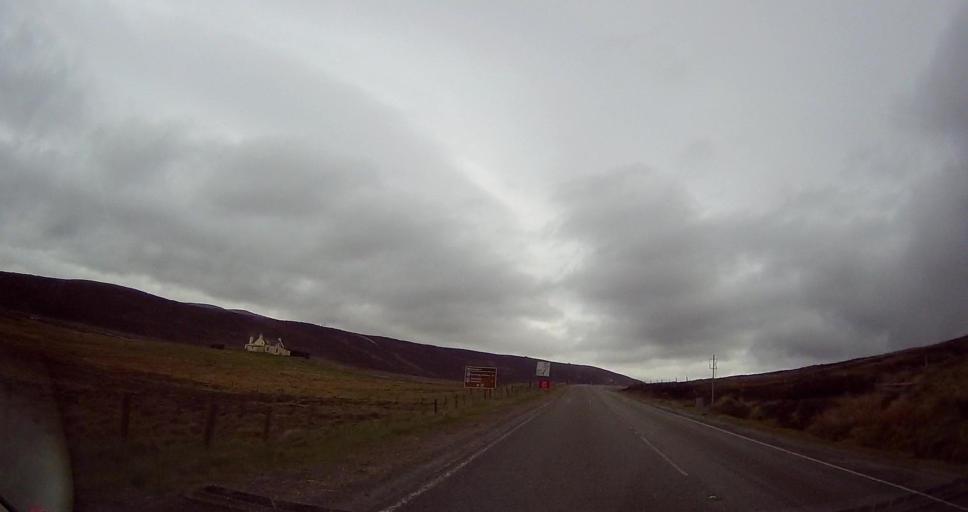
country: GB
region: Scotland
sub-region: Shetland Islands
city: Lerwick
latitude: 60.2767
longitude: -1.2431
